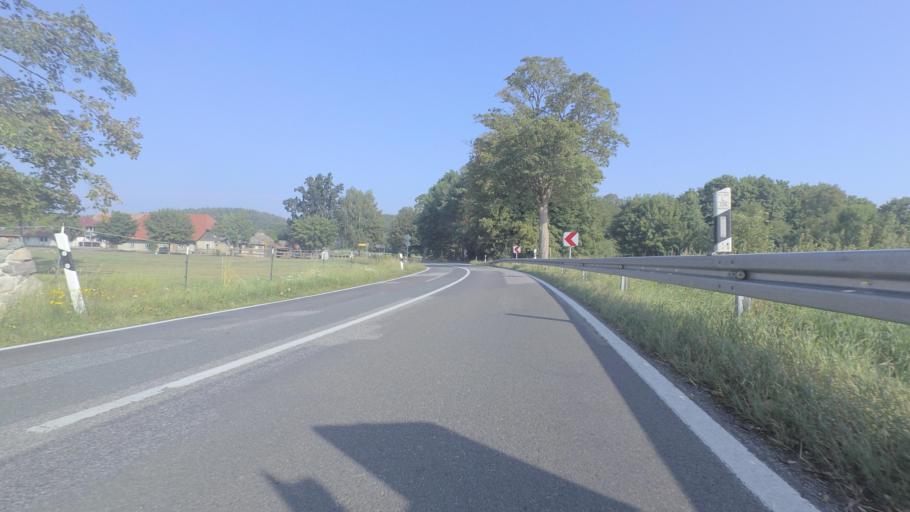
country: DE
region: Mecklenburg-Vorpommern
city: Malchow
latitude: 53.4458
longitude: 12.4326
